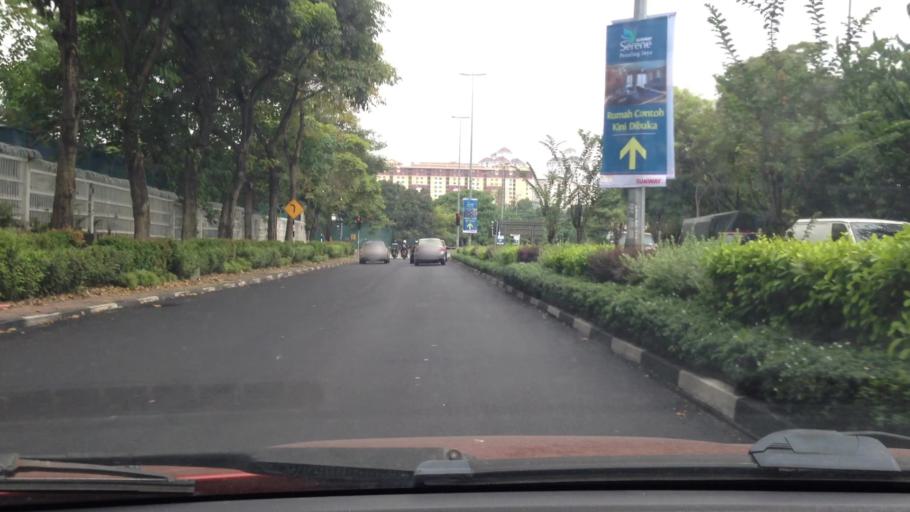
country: MY
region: Selangor
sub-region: Petaling
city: Petaling Jaya
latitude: 3.0886
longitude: 101.6071
